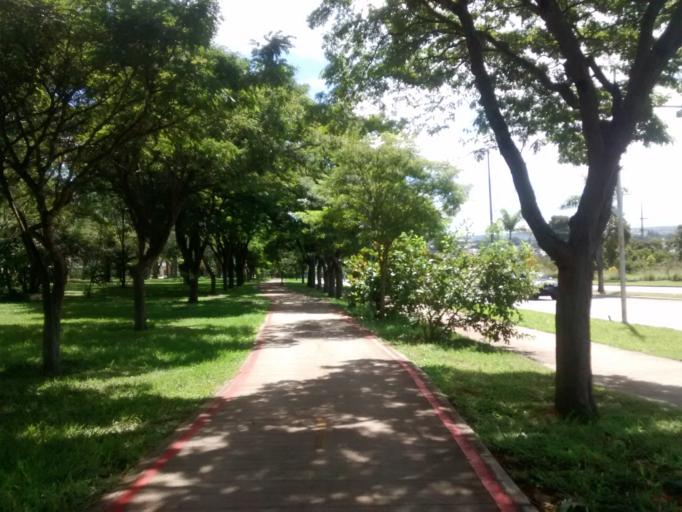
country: BR
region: Federal District
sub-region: Brasilia
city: Brasilia
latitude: -15.7386
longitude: -47.8850
